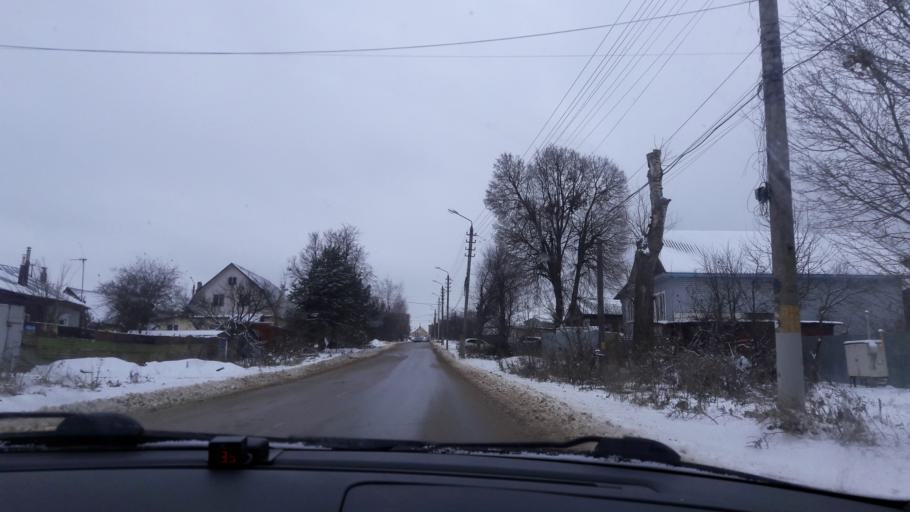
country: RU
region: Tula
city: Gorelki
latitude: 54.2339
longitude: 37.6355
